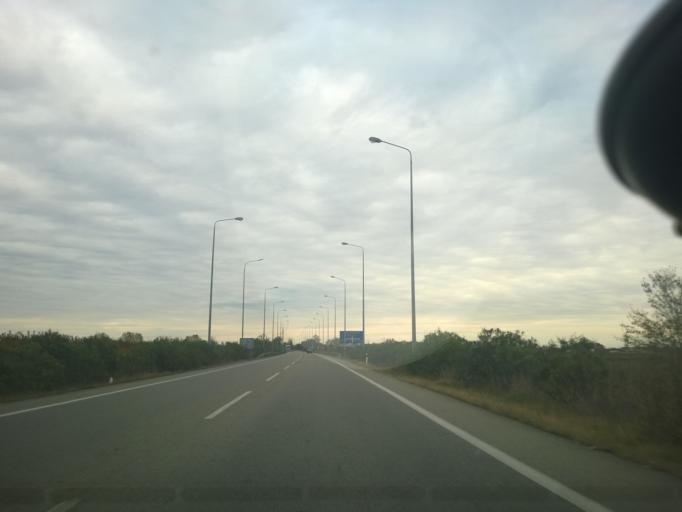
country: GR
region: Central Macedonia
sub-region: Nomos Pellis
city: Karyotissa
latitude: 40.7796
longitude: 22.3091
